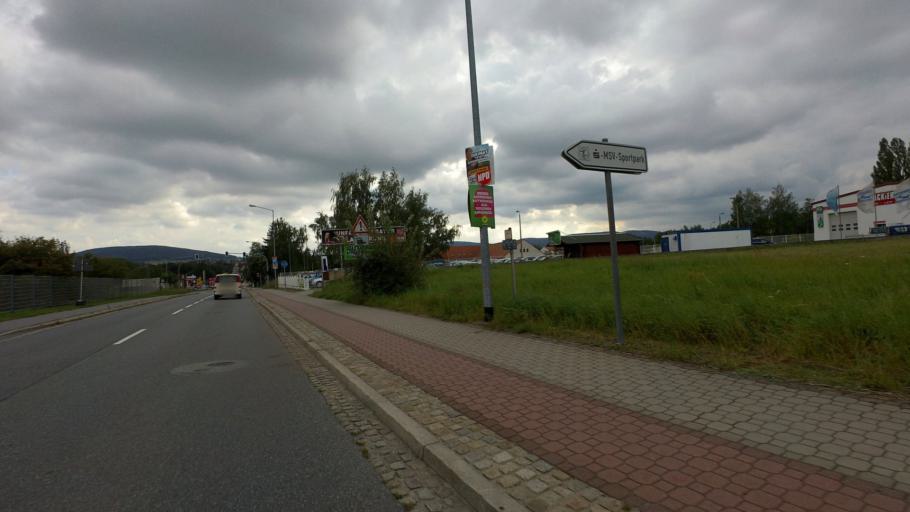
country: DE
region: Saxony
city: Bautzen
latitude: 51.1667
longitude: 14.4267
